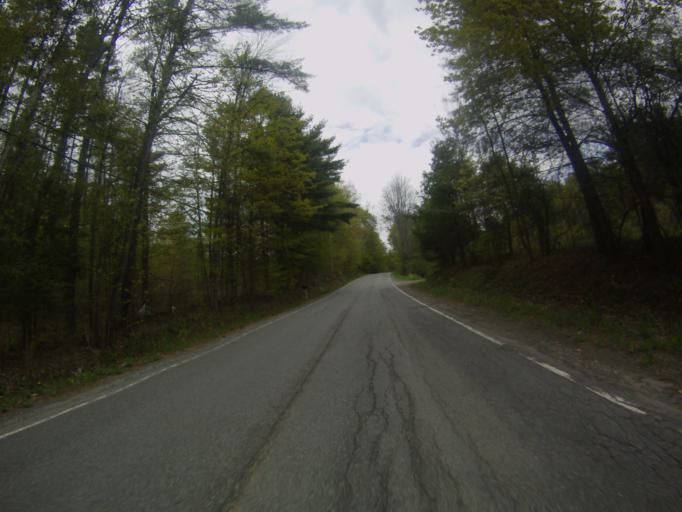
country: US
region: New York
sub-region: Essex County
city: Port Henry
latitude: 43.9636
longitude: -73.4893
